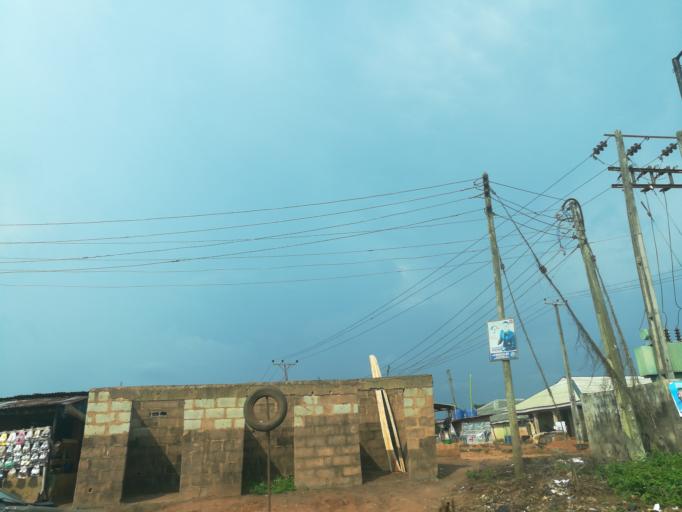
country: NG
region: Lagos
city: Ikorodu
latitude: 6.6644
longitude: 3.6663
